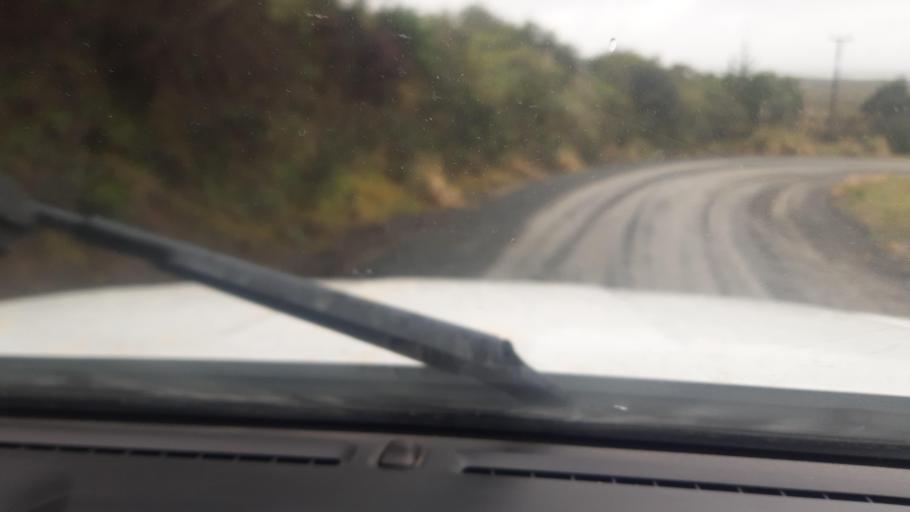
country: NZ
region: Northland
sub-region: Far North District
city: Kaitaia
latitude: -34.9914
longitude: 173.2143
